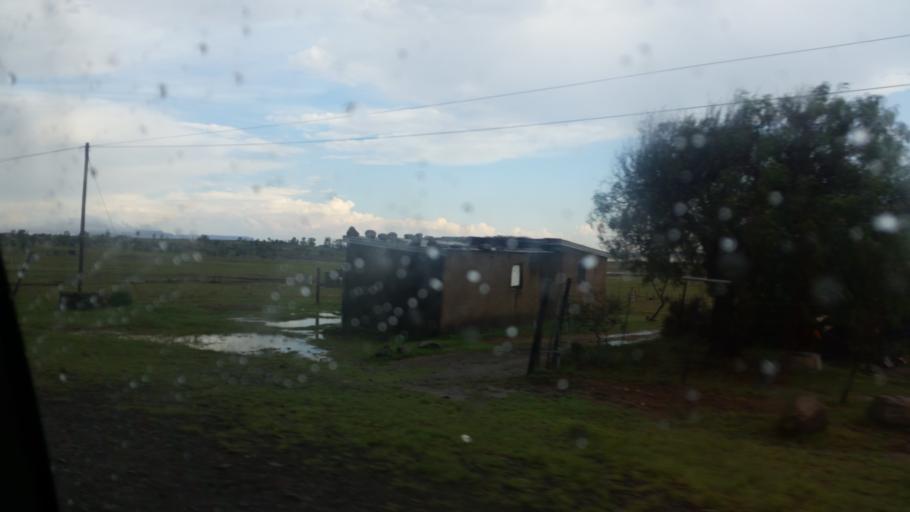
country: LS
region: Mafeteng
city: Mafeteng
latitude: -29.7569
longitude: 27.1156
